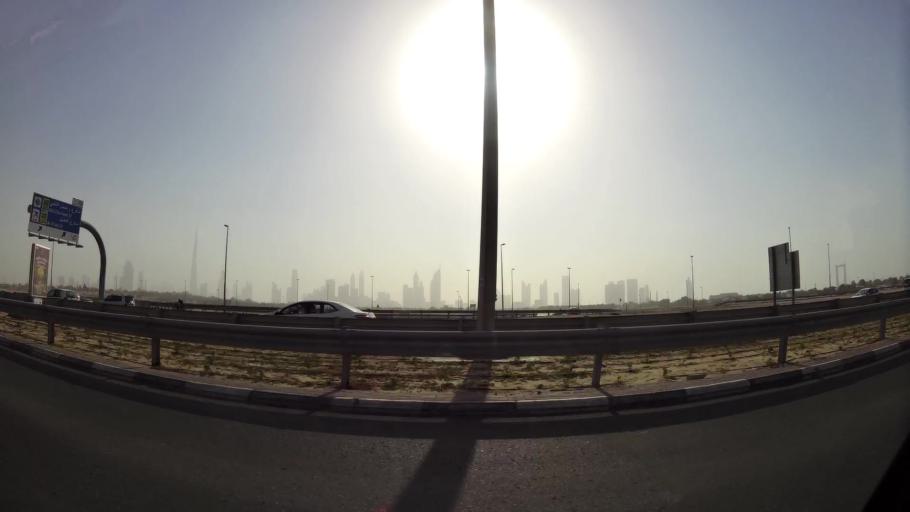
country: AE
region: Ash Shariqah
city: Sharjah
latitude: 25.2155
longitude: 55.3142
